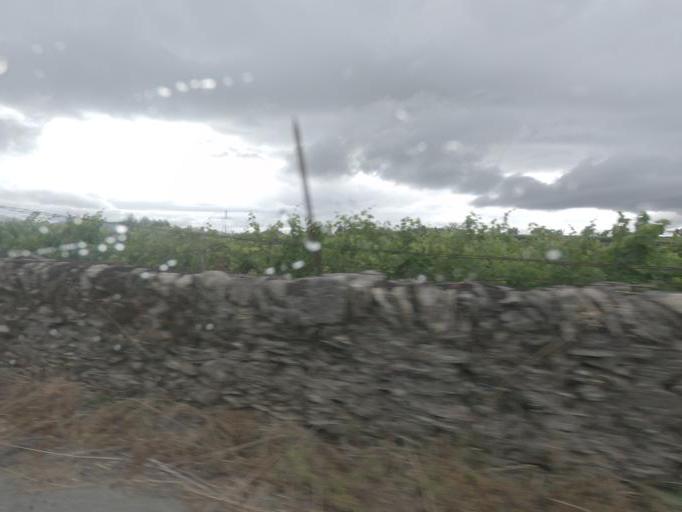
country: PT
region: Vila Real
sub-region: Sabrosa
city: Sabrosa
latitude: 41.2479
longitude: -7.4981
